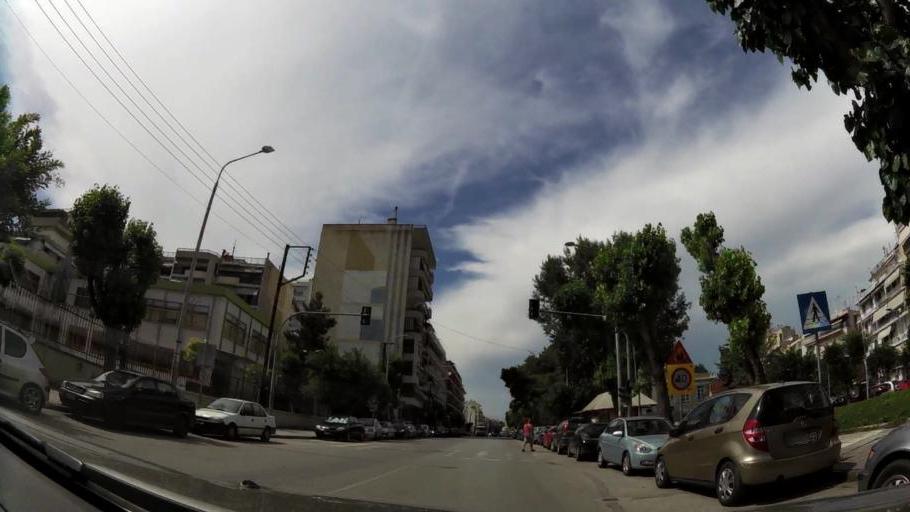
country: GR
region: Central Macedonia
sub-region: Nomos Thessalonikis
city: Triandria
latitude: 40.6027
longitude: 22.9586
